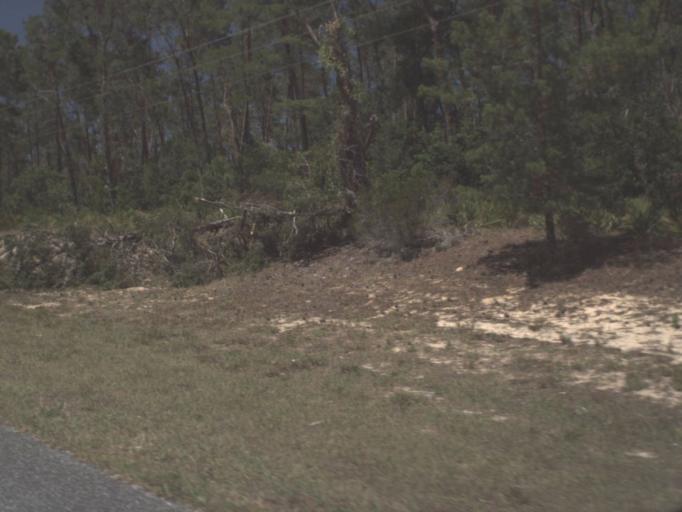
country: US
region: Florida
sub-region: Lake County
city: Astor
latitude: 29.1458
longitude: -81.6309
